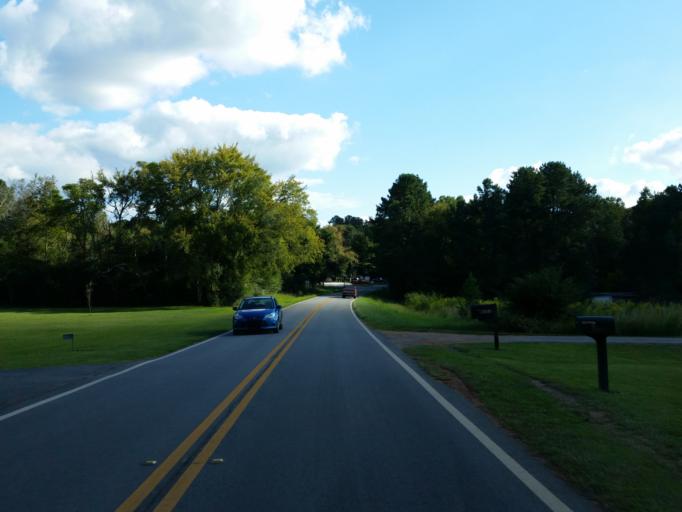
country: US
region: Georgia
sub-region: Butts County
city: Indian Springs
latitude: 33.1909
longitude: -84.0055
